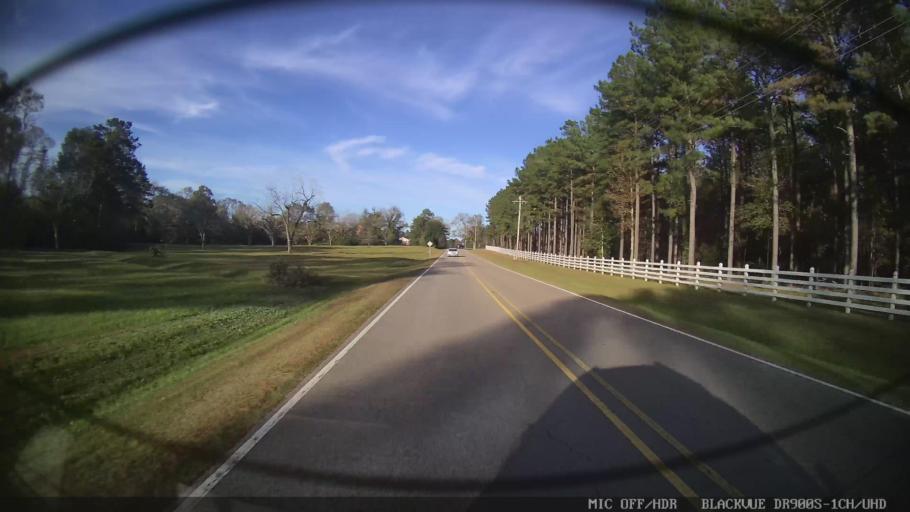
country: US
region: Mississippi
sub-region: Lamar County
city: Purvis
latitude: 31.1843
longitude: -89.2914
